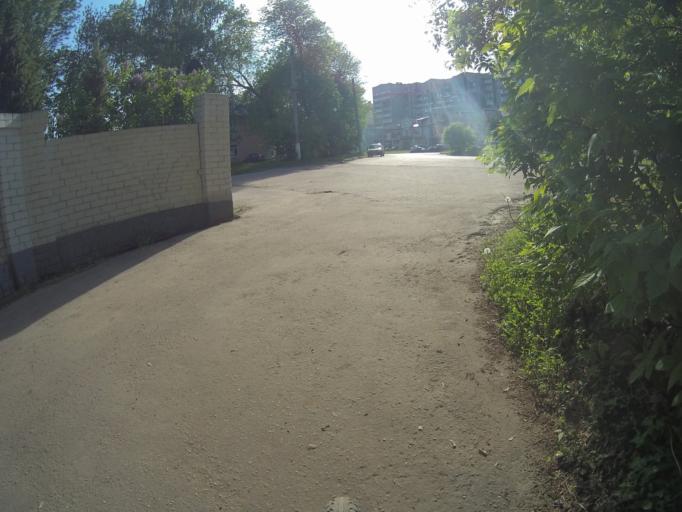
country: RU
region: Vladimir
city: Bogolyubovo
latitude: 56.1684
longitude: 40.4866
